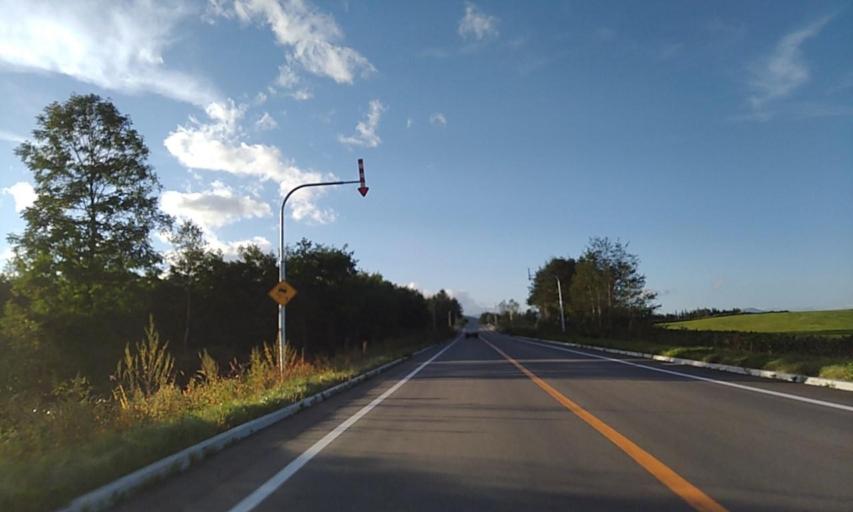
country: JP
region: Hokkaido
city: Otofuke
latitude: 42.9783
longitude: 142.8657
